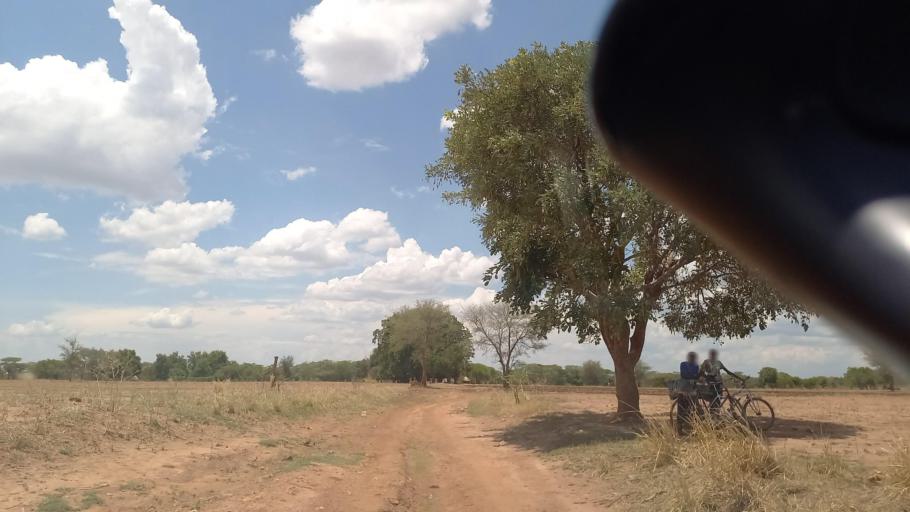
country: ZM
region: Southern
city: Mazabuka
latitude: -16.1123
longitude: 27.8148
